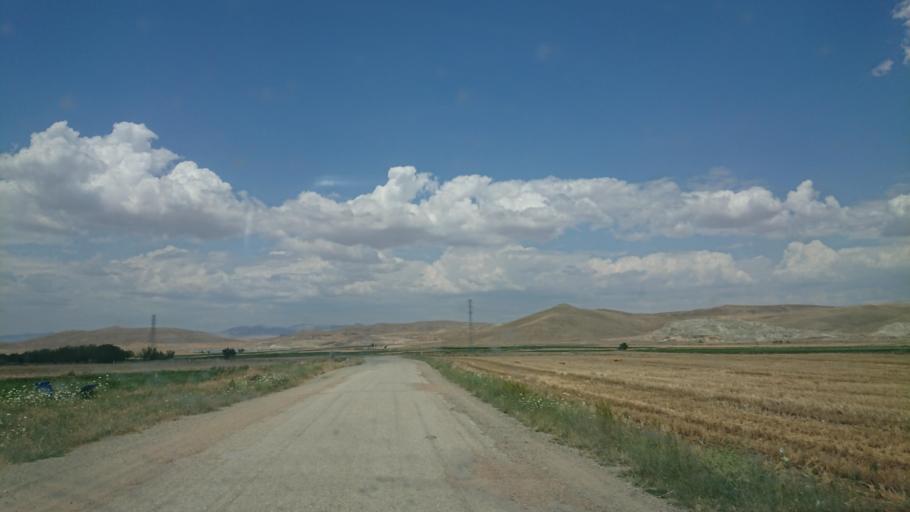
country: TR
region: Aksaray
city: Sariyahsi
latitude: 38.9791
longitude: 33.9028
